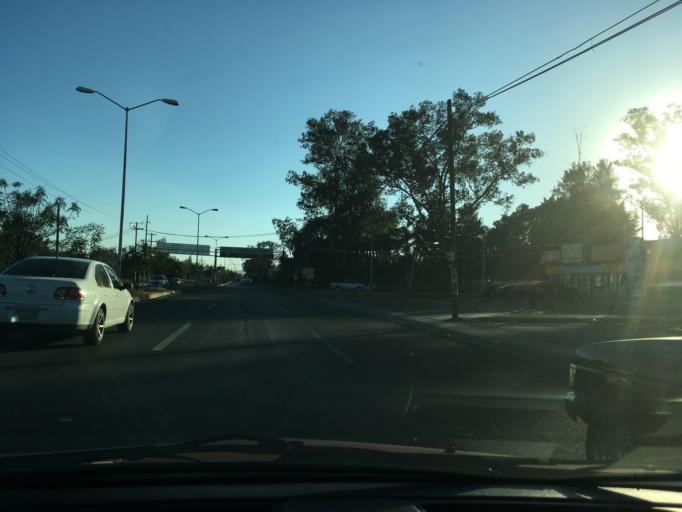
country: MX
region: Jalisco
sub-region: Tlajomulco de Zuniga
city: La Tijera
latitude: 20.5799
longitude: -103.4294
